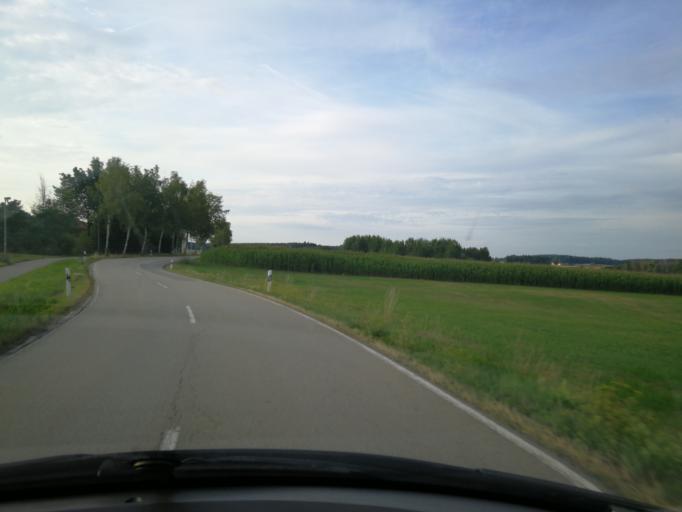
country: DE
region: Bavaria
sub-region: Lower Bavaria
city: Wiesenfelden
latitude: 49.0438
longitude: 12.5334
